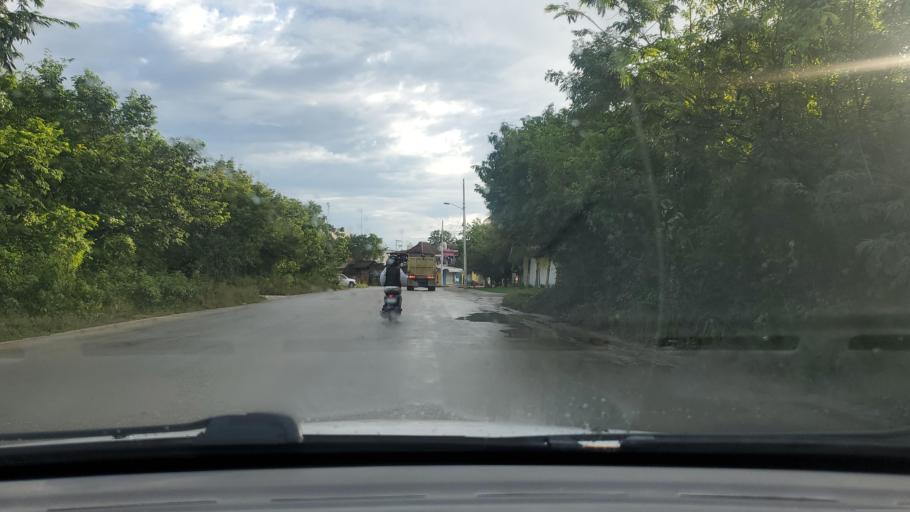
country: MX
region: Quintana Roo
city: Tulum
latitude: 20.2107
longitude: -87.4749
